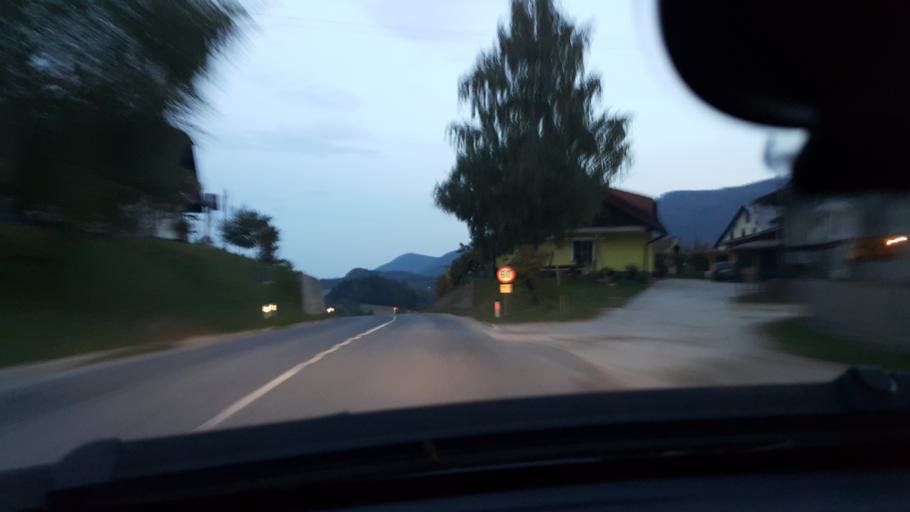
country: SI
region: Zrece
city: Zrece
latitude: 46.3677
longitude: 15.3505
